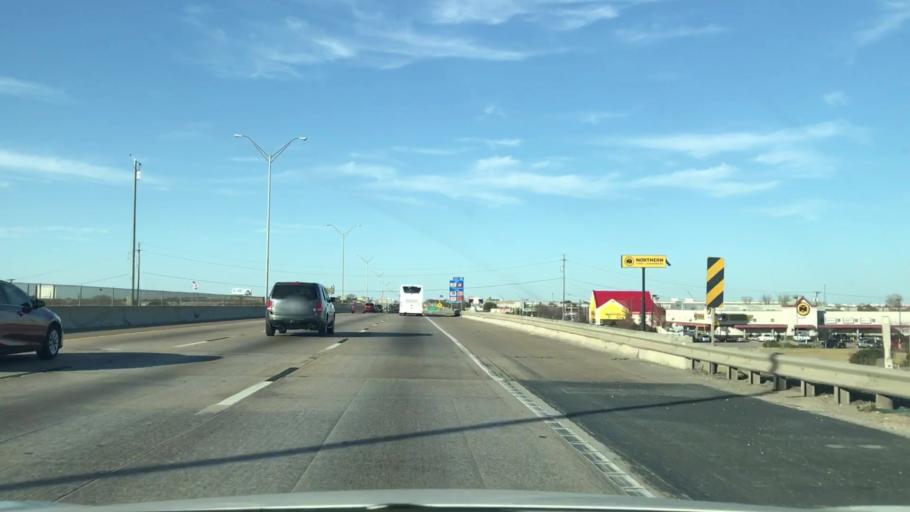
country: US
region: Texas
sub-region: Tarrant County
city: Everman
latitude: 32.6134
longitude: -97.3216
